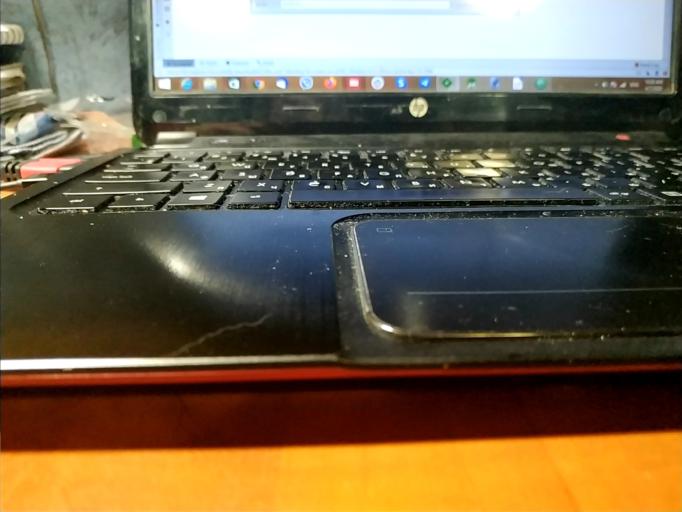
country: RU
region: Vologda
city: Suda
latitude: 58.9171
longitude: 37.5432
